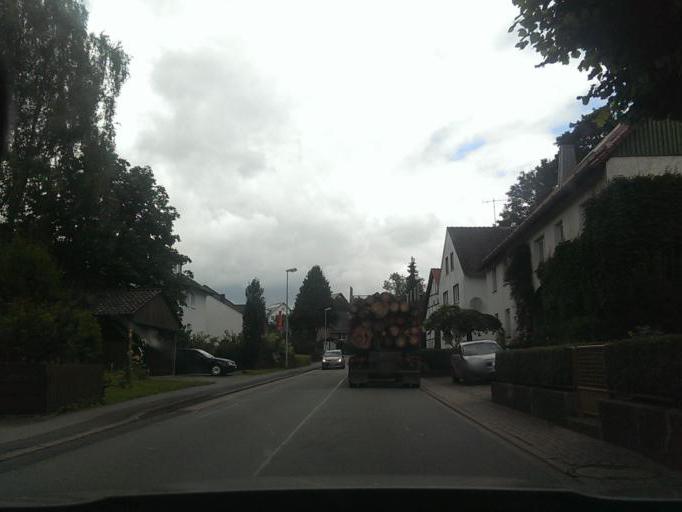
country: DE
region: North Rhine-Westphalia
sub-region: Regierungsbezirk Detmold
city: Hoexter
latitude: 51.8351
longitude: 9.3420
